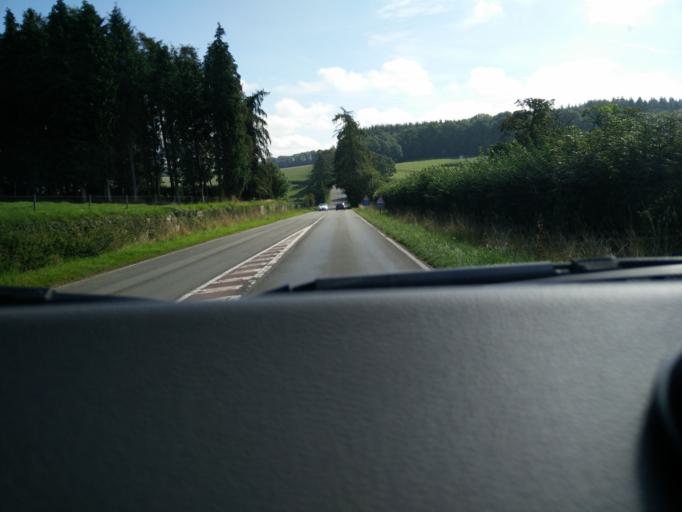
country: BE
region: Wallonia
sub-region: Province de Namur
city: Dinant
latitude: 50.2596
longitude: 4.9842
